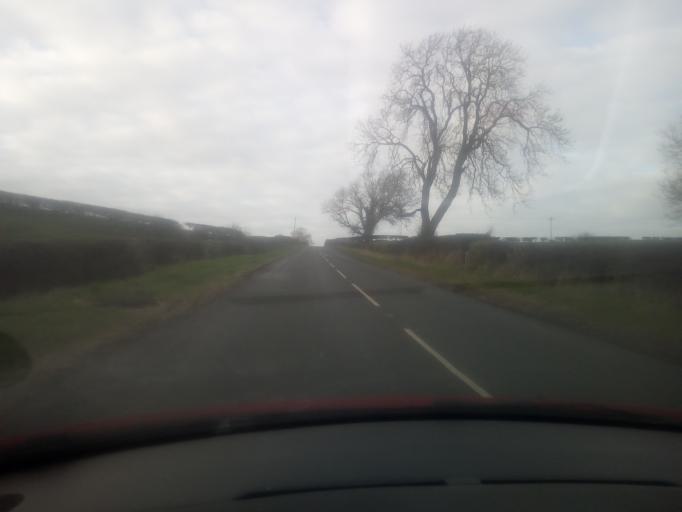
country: GB
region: England
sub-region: Darlington
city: Summerhouse
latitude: 54.5950
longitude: -1.6807
